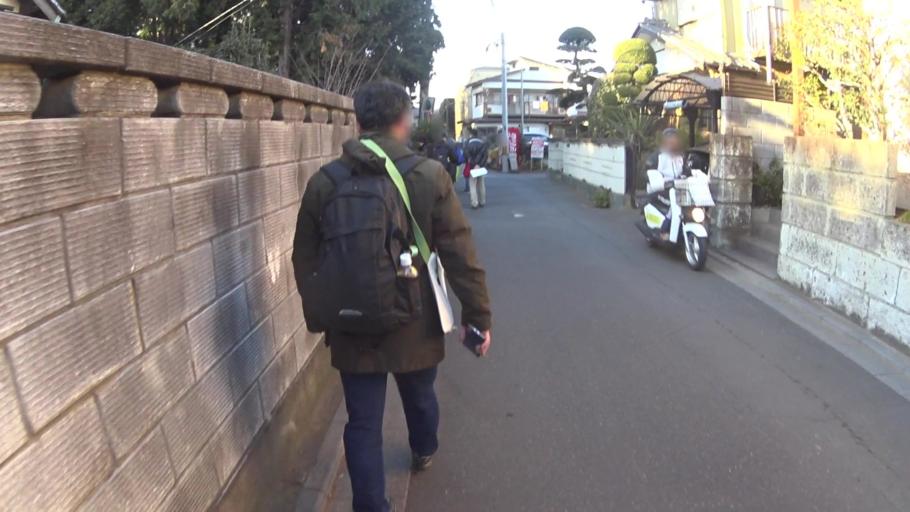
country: JP
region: Saitama
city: Shimotoda
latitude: 35.8508
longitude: 139.6887
